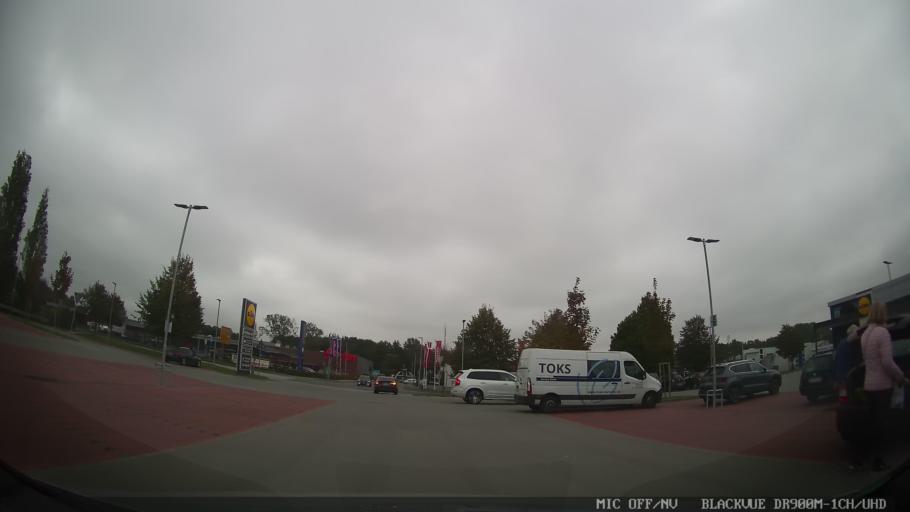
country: DE
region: Schleswig-Holstein
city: Heiligenhafen
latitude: 54.3657
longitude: 11.0081
